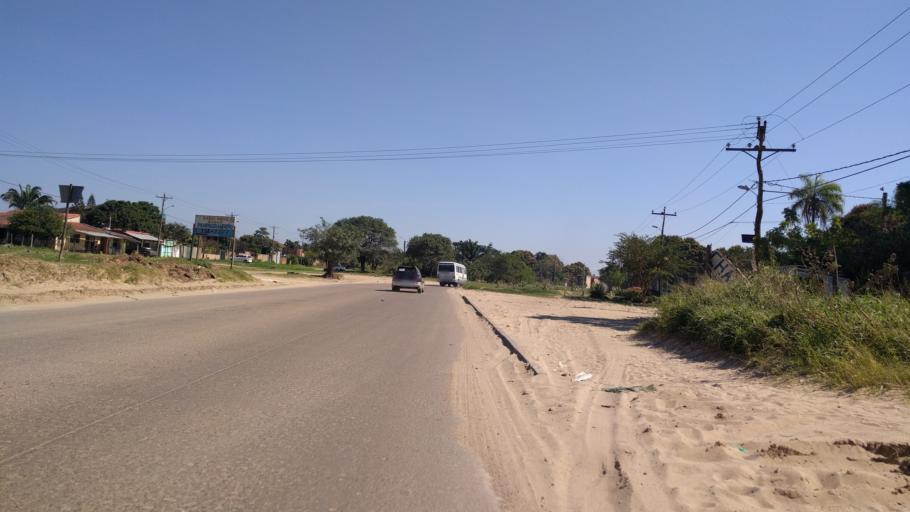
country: BO
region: Santa Cruz
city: Santa Cruz de la Sierra
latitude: -17.8412
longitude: -63.2175
